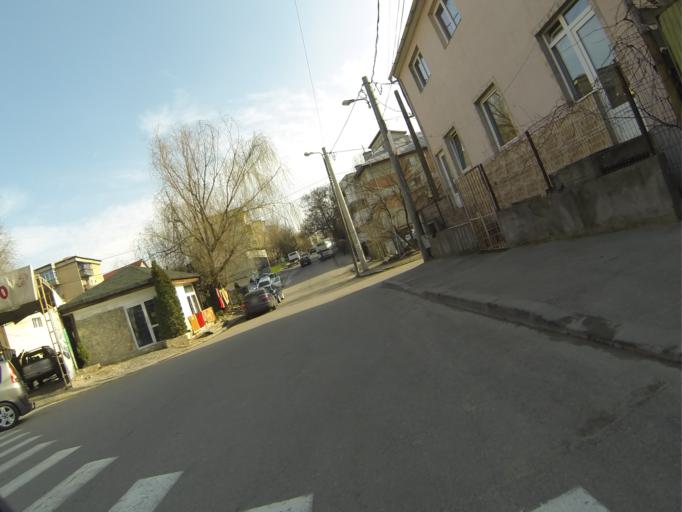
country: RO
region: Dolj
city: Craiova
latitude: 44.3076
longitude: 23.8141
